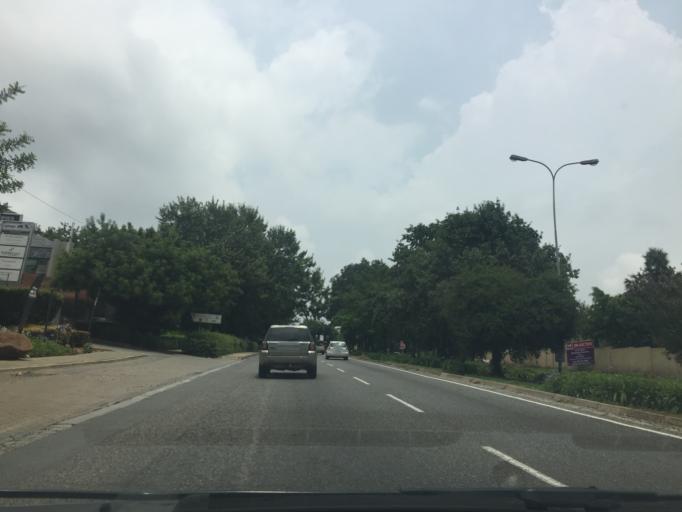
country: ZA
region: Gauteng
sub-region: City of Johannesburg Metropolitan Municipality
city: Modderfontein
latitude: -26.1007
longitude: 28.0655
